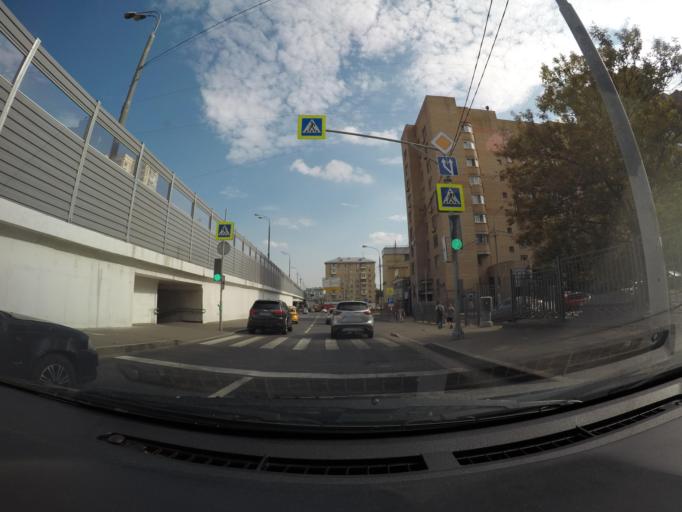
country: RU
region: Moscow
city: Sokol'niki
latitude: 55.7821
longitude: 37.6675
